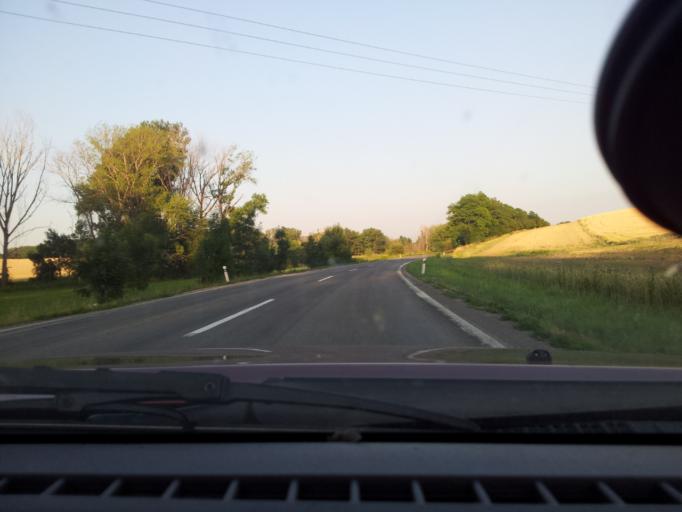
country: SK
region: Trnavsky
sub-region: Okres Skalica
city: Skalica
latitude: 48.7664
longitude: 17.2937
